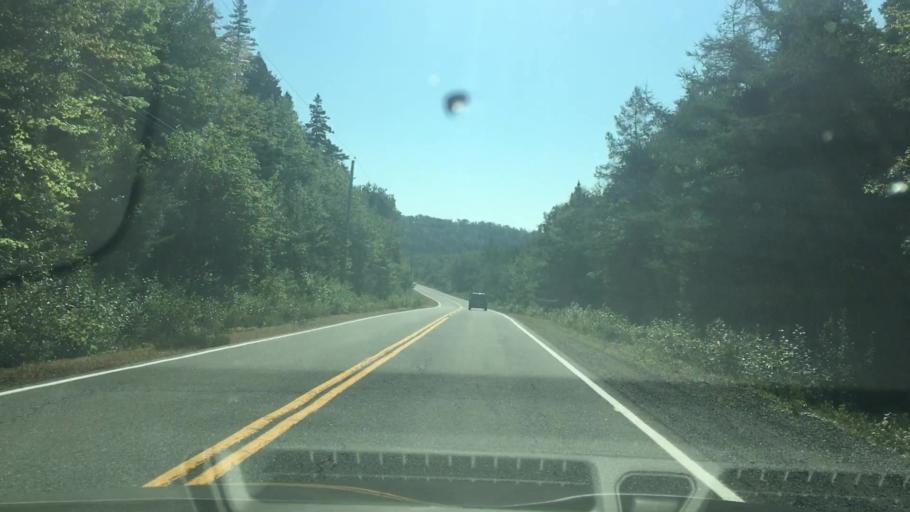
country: CA
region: Nova Scotia
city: Cole Harbour
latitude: 44.8075
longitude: -62.8331
